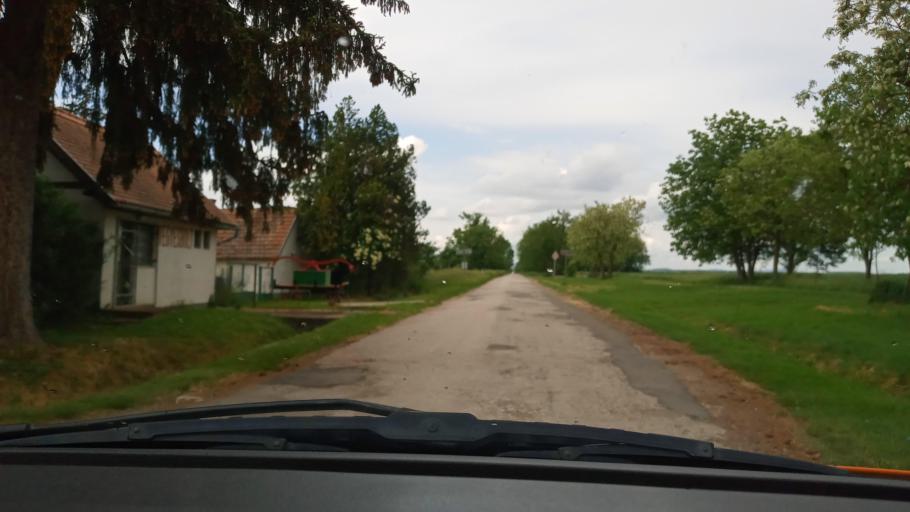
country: HU
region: Baranya
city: Harkany
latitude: 45.9002
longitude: 18.1368
